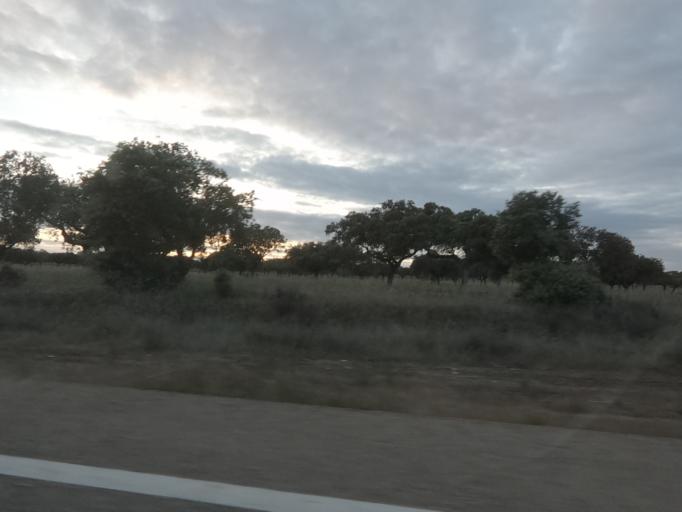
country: ES
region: Extremadura
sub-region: Provincia de Badajoz
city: Villar del Rey
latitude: 39.0375
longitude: -6.8172
